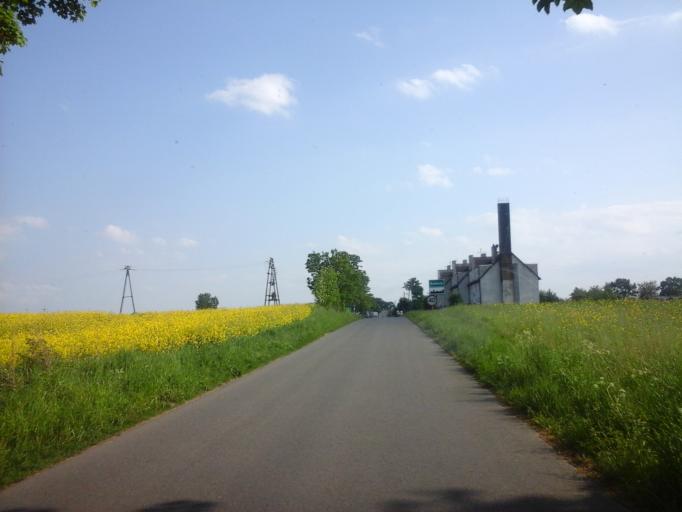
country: PL
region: West Pomeranian Voivodeship
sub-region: Powiat choszczenski
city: Pelczyce
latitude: 53.0782
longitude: 15.3738
